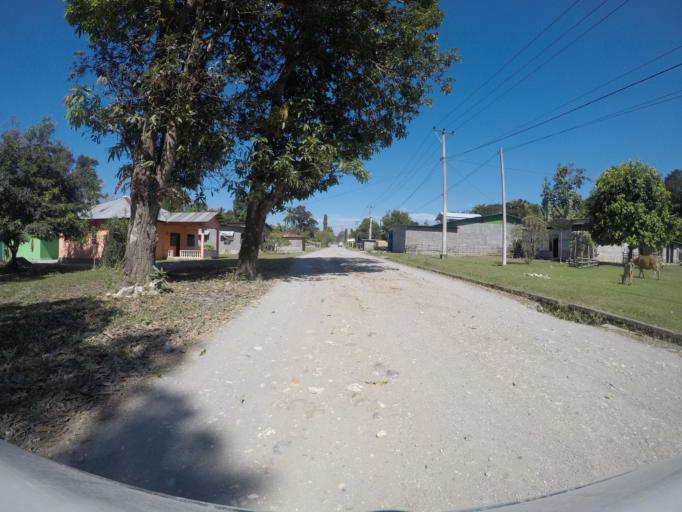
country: TL
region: Viqueque
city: Viqueque
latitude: -8.9761
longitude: 126.0461
